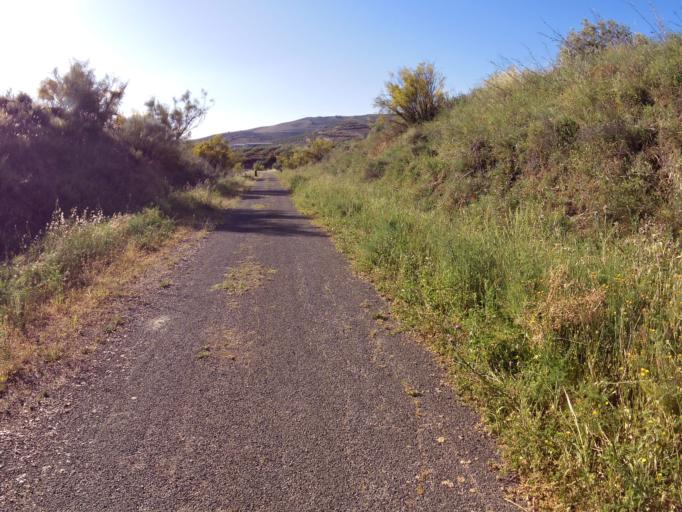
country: ES
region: Andalusia
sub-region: Province of Cordoba
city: Luque
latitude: 37.5660
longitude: -4.2466
